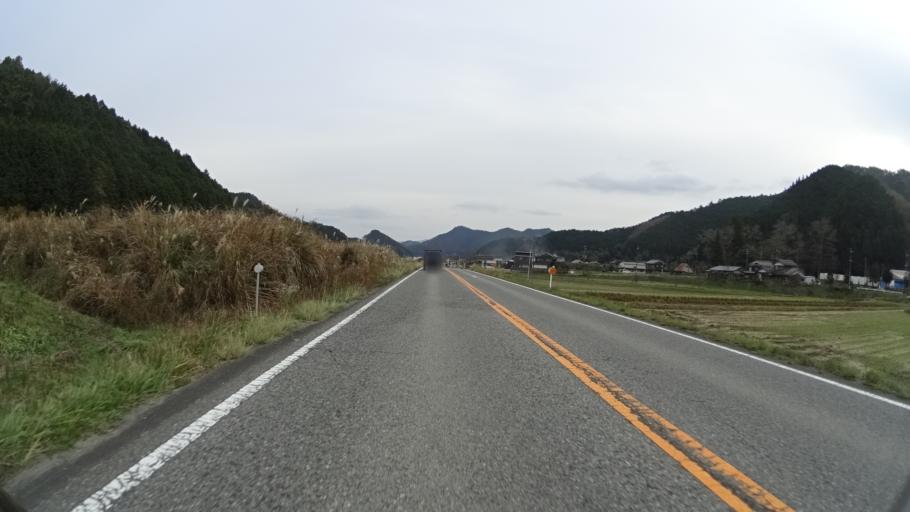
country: JP
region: Hyogo
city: Sasayama
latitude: 35.1079
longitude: 135.1239
